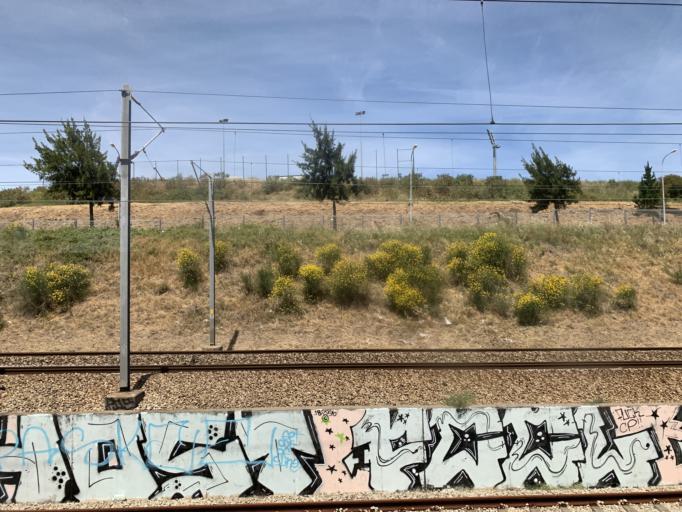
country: PT
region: Lisbon
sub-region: Sintra
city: Queluz
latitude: 38.7509
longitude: -9.2677
